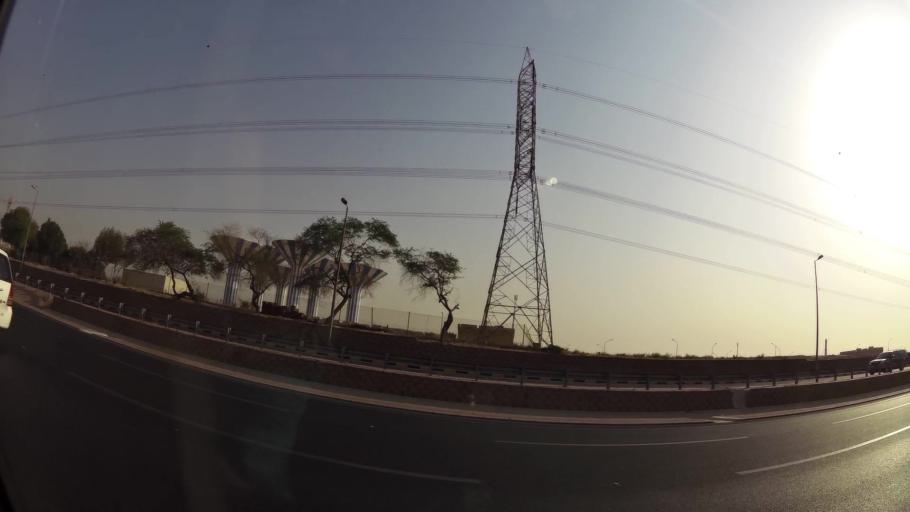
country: KW
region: Al Farwaniyah
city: Janub as Surrah
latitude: 29.3049
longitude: 47.9947
